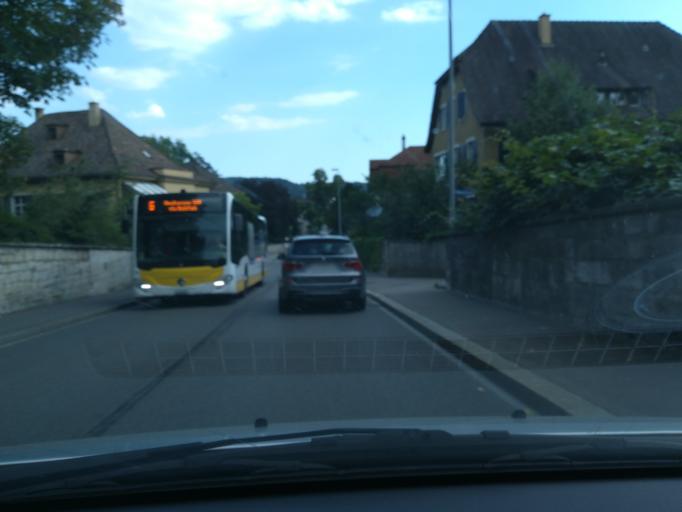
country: CH
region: Schaffhausen
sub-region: Bezirk Schaffhausen
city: Schaffhausen
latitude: 47.6993
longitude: 8.6272
